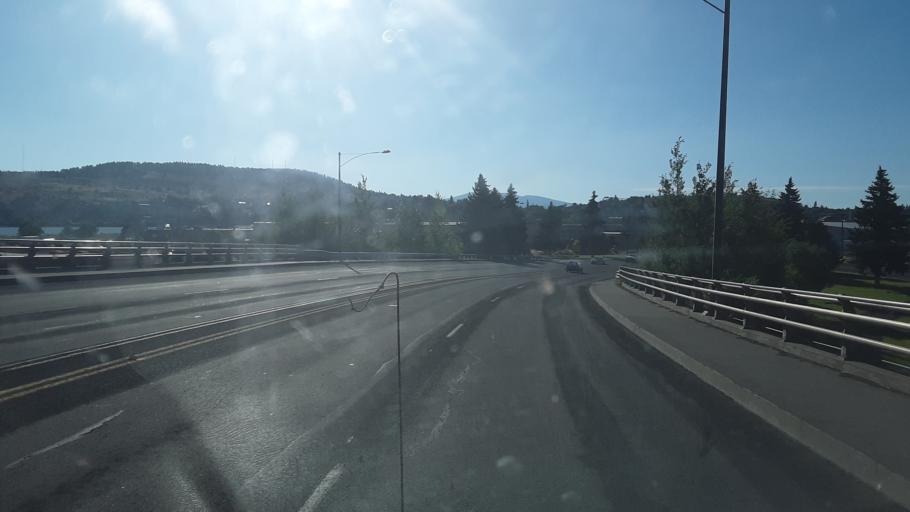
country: US
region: Oregon
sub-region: Klamath County
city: Klamath Falls
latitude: 42.2186
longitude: -121.7723
